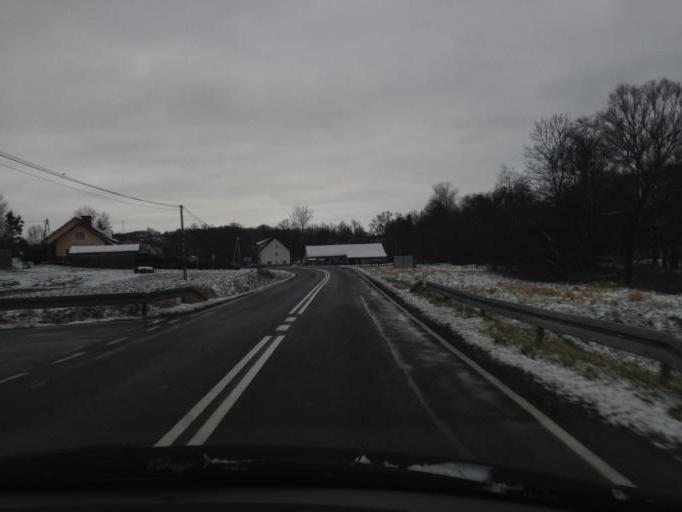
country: PL
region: Lesser Poland Voivodeship
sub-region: Powiat tarnowski
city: Rzepiennik Strzyzewski
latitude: 49.8093
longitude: 21.0228
